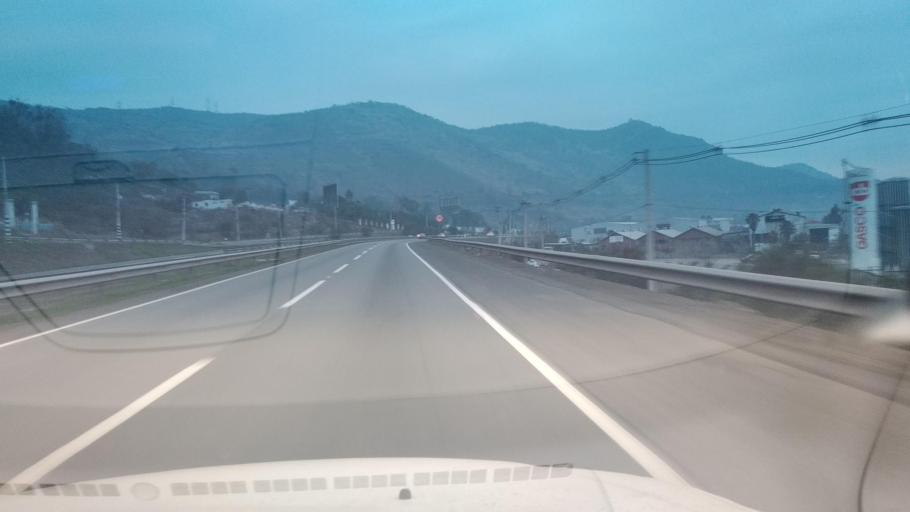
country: CL
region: Santiago Metropolitan
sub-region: Provincia de Chacabuco
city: Chicureo Abajo
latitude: -33.3319
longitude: -70.6958
